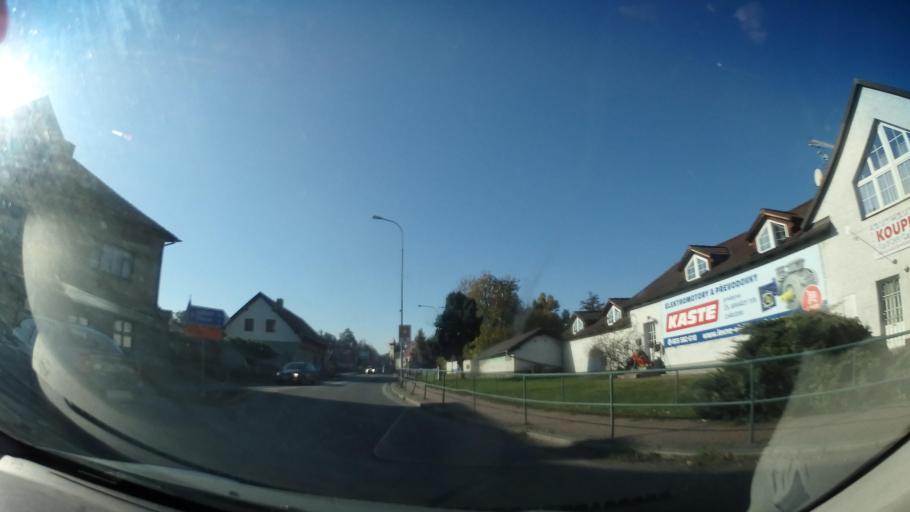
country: CZ
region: Pardubicky
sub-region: Okres Chrudim
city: Slatinany
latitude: 49.9214
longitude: 15.8132
